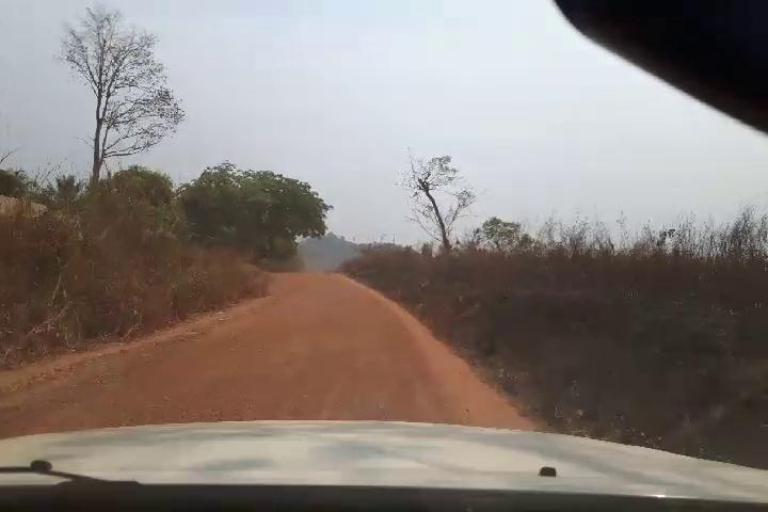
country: SL
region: Northern Province
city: Bumbuna
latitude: 9.0323
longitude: -11.7621
